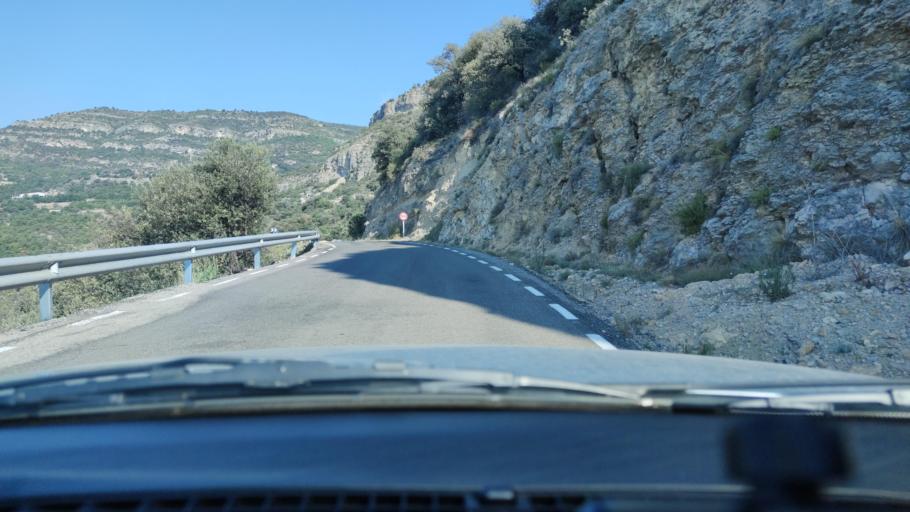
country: ES
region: Catalonia
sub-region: Provincia de Lleida
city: Llimiana
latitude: 42.0830
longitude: 0.8571
